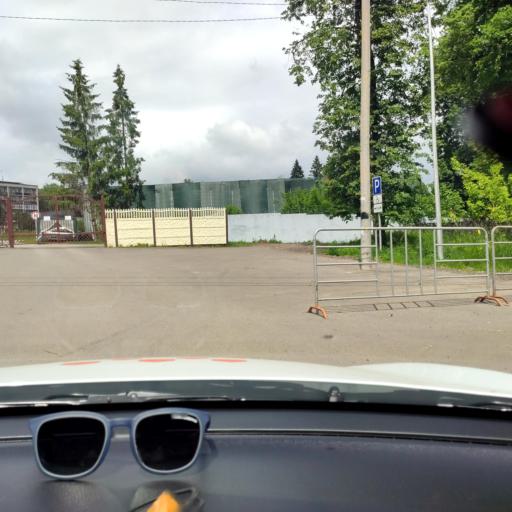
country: RU
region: Tatarstan
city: Vysokaya Gora
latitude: 55.9284
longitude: 49.2019
